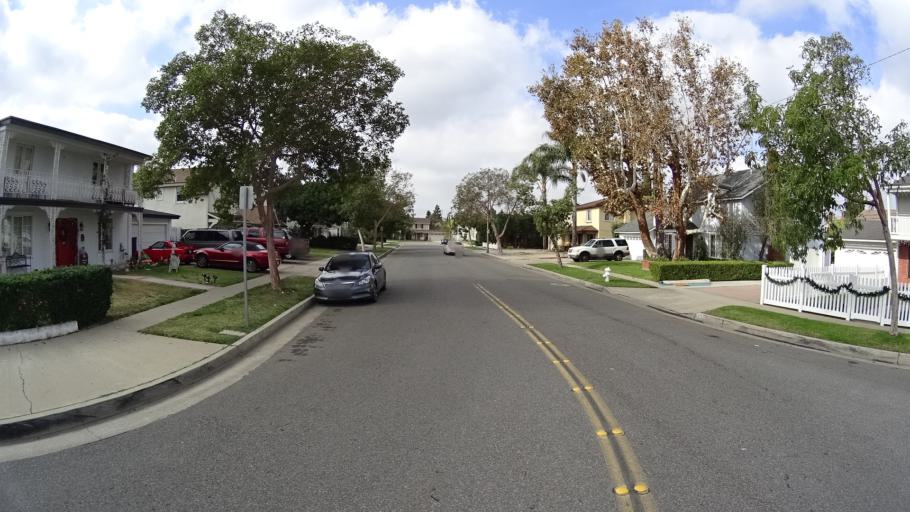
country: US
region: California
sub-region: Orange County
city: Tustin
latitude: 33.7657
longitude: -117.8320
